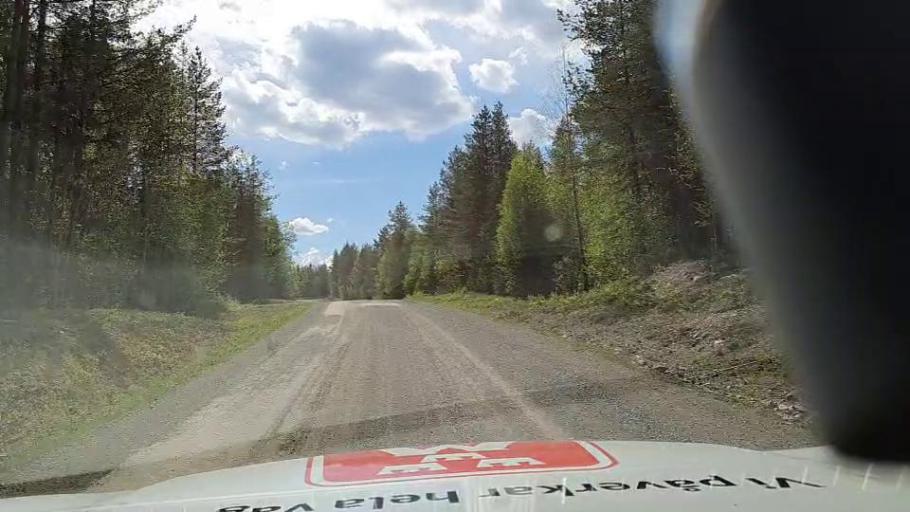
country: SE
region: Vaesterbotten
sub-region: Vilhelmina Kommun
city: Sjoberg
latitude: 64.5714
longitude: 15.8618
